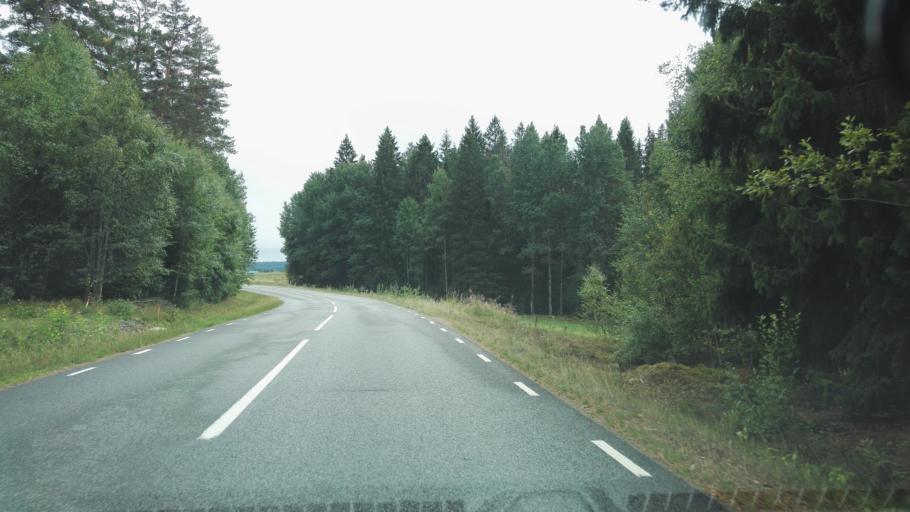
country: SE
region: Joenkoeping
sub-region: Vetlanda Kommun
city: Landsbro
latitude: 57.2299
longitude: 14.9455
